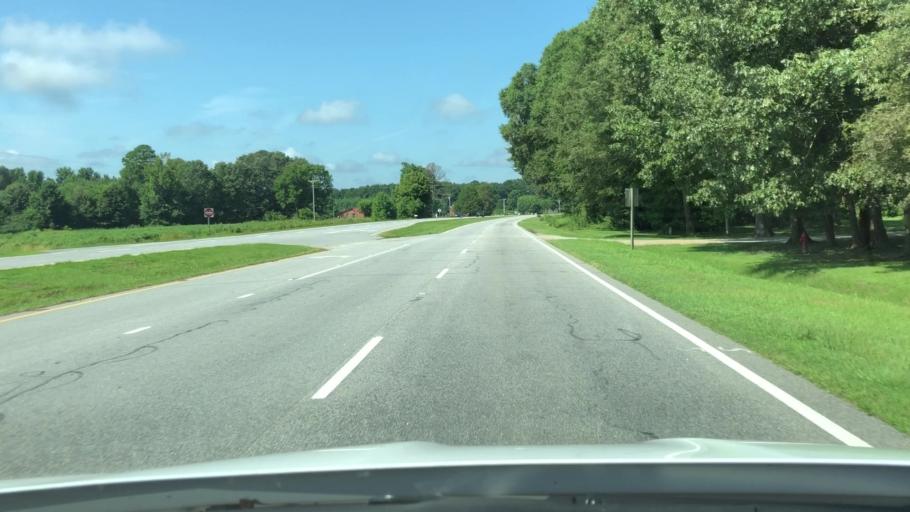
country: US
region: North Carolina
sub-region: Bertie County
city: Windsor
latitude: 35.9361
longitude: -76.9737
